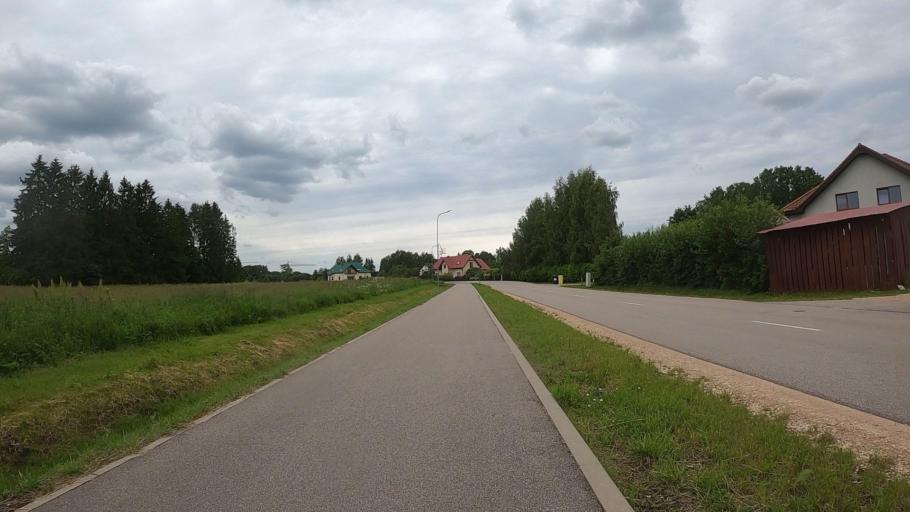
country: LV
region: Babite
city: Pinki
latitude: 56.8776
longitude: 23.9689
